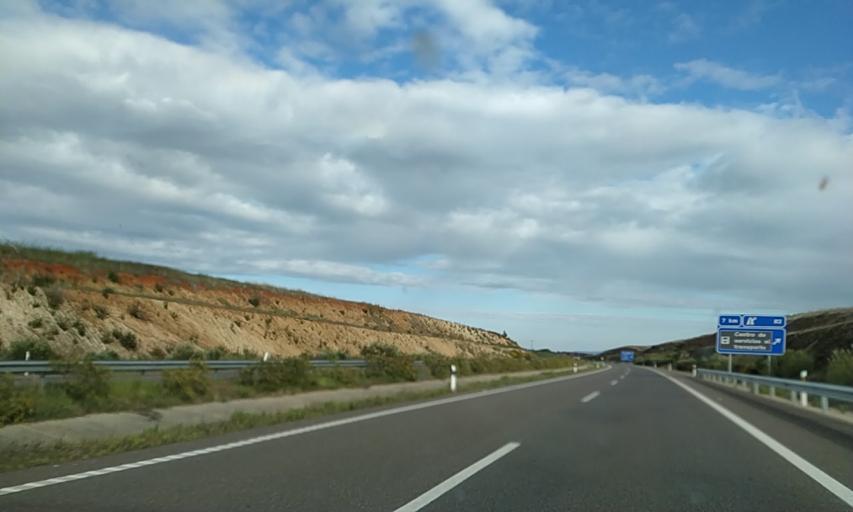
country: ES
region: Extremadura
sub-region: Provincia de Caceres
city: Casas de Don Gomez
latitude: 40.0144
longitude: -6.5823
